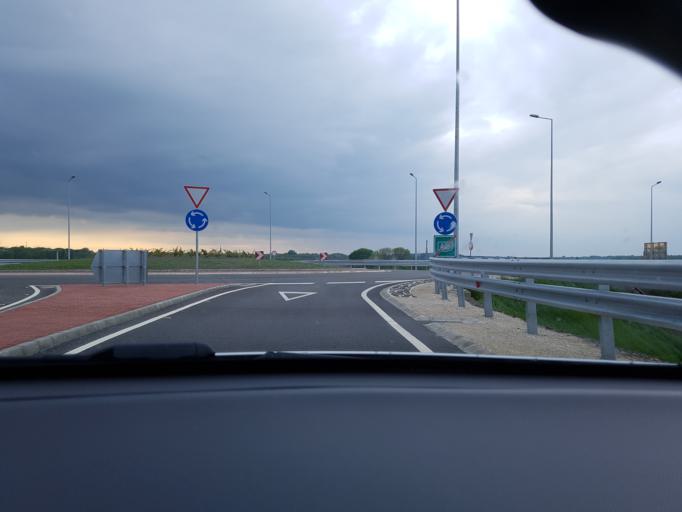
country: HU
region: Bacs-Kiskun
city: Kecskemet
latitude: 46.9331
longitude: 19.6163
